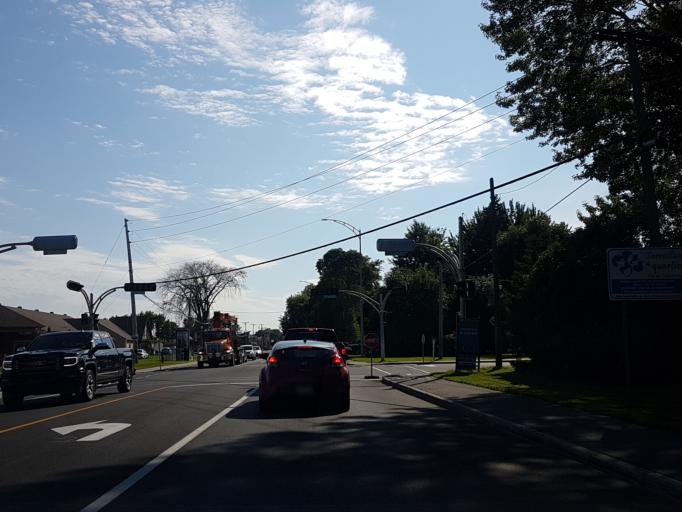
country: CA
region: Quebec
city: Sainte-Catherine
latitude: 46.3115
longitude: -72.5790
